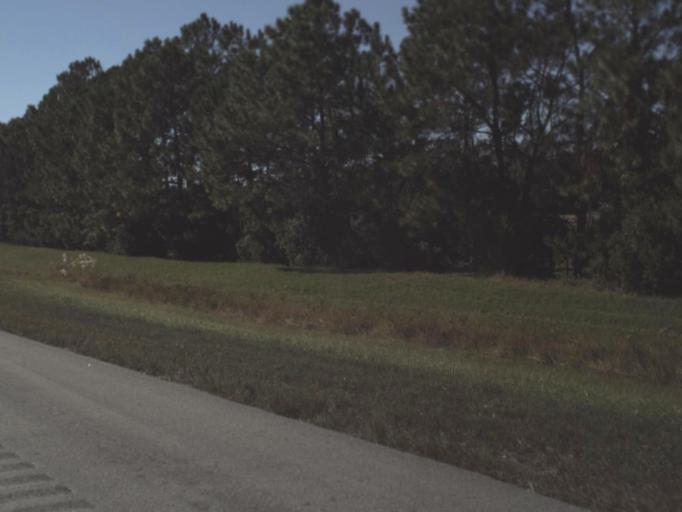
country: US
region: Florida
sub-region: Seminole County
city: Goldenrod
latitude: 28.6272
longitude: -81.2488
